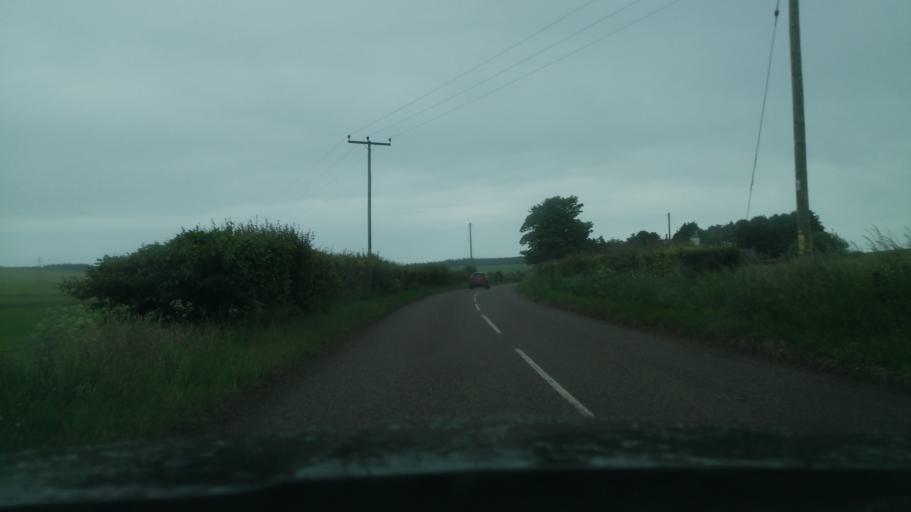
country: GB
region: Scotland
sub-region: Moray
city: Cullen
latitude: 57.6448
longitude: -2.8307
